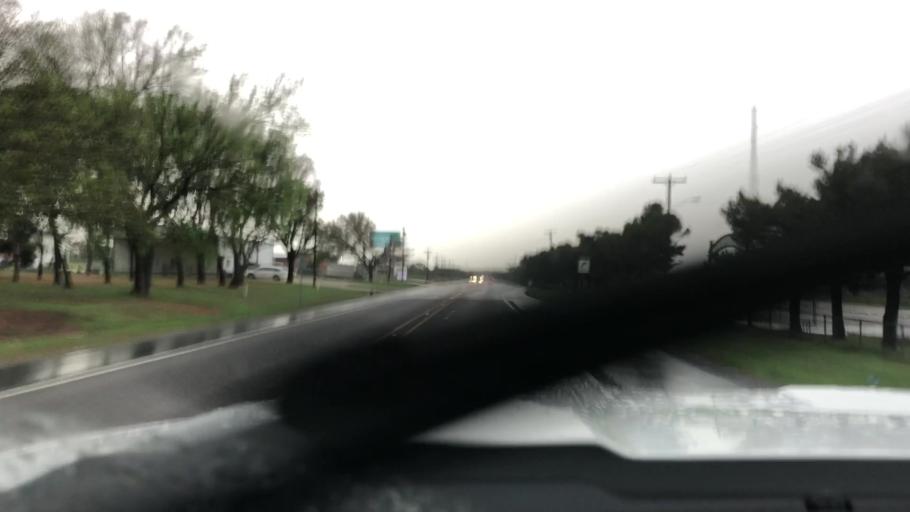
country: US
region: Texas
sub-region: Johnson County
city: Keene
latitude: 32.4071
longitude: -97.3251
